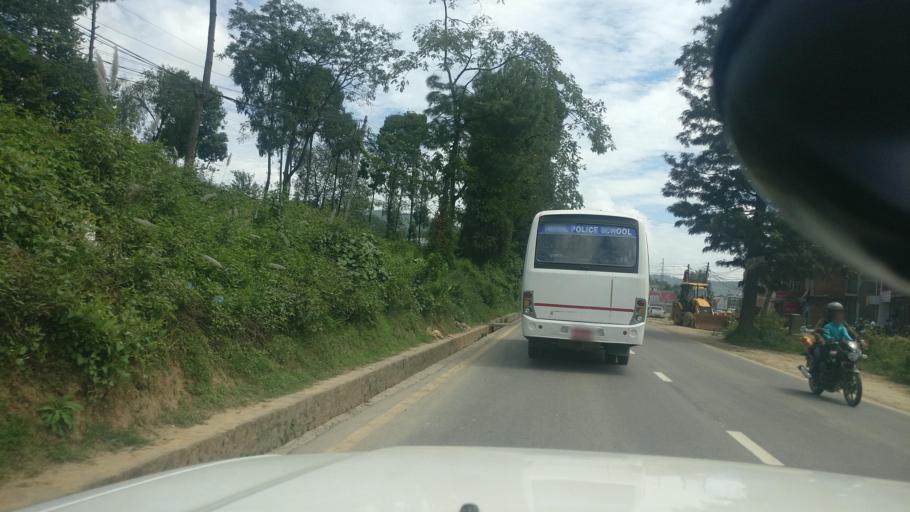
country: NP
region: Central Region
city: Banepa
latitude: 27.6320
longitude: 85.5000
